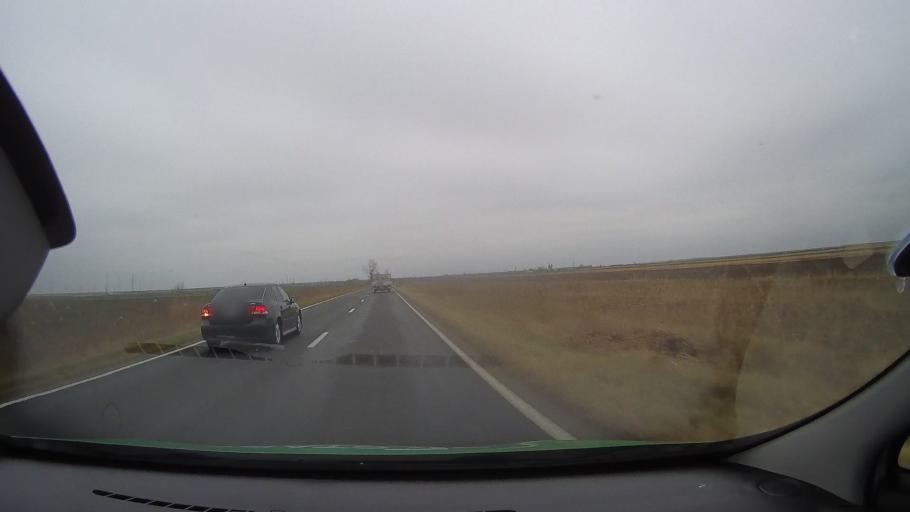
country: RO
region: Ialomita
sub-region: Comuna Scanteia
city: Scanteia
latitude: 44.7439
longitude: 27.4427
